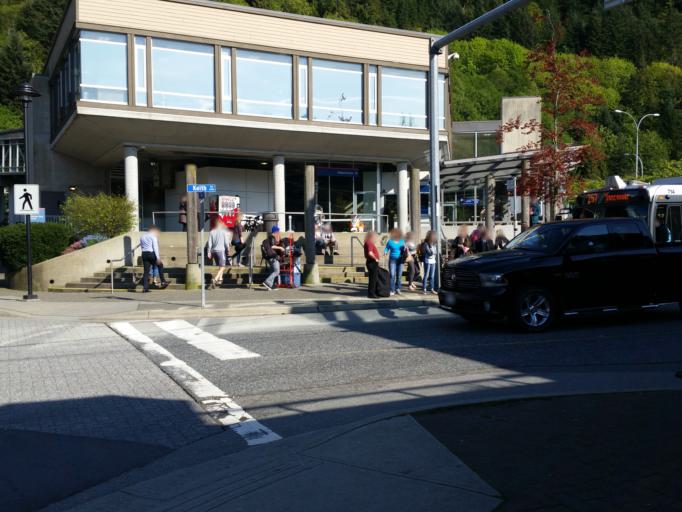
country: CA
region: British Columbia
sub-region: Greater Vancouver Regional District
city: Bowen Island
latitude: 49.3743
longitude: -123.2731
